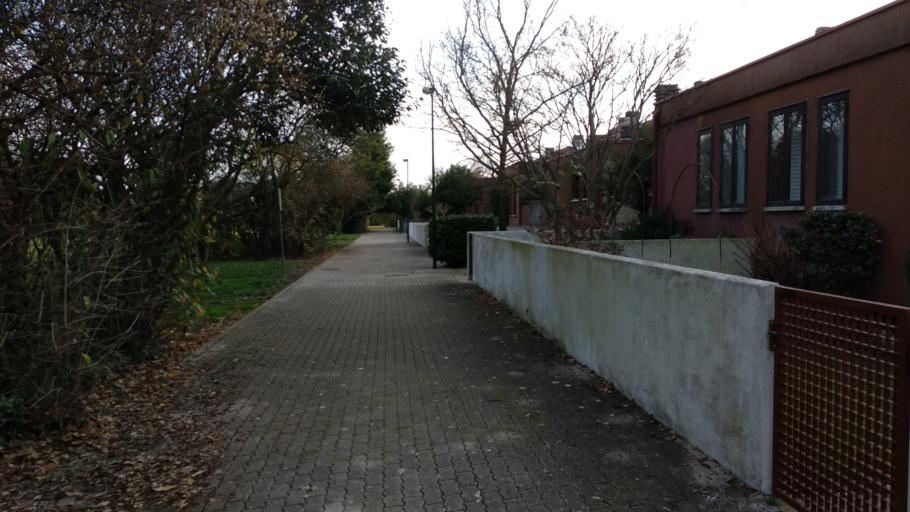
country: IT
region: Veneto
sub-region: Provincia di Venezia
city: Campalto
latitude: 45.4839
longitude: 12.2689
